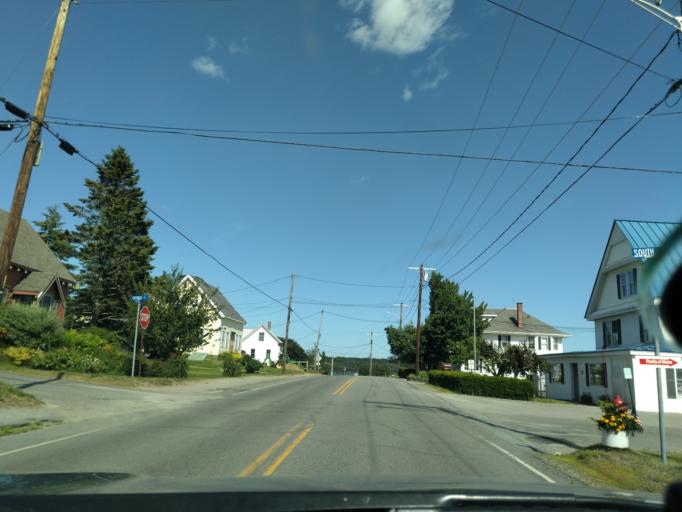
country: US
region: Maine
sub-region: Washington County
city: Eastport
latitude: 44.8580
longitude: -66.9872
